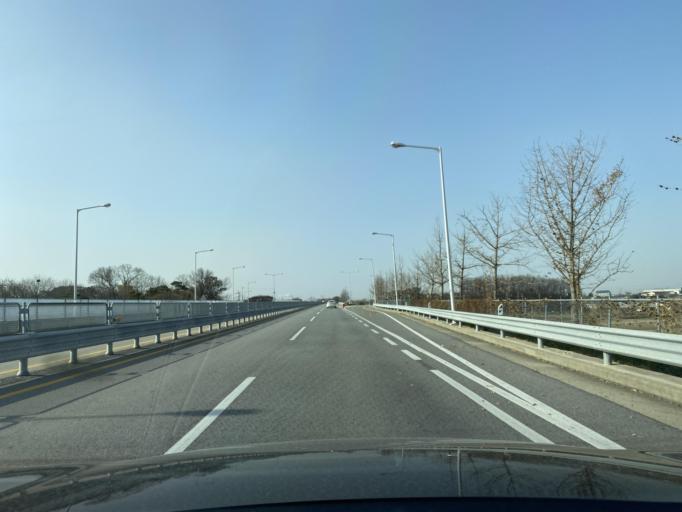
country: KR
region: Chungcheongnam-do
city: Yesan
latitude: 36.7578
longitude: 126.8242
